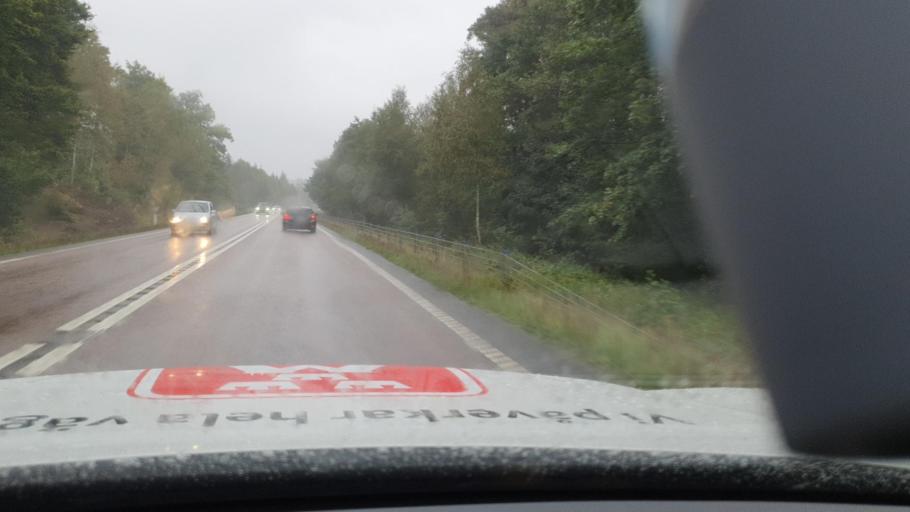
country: SE
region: Skane
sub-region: Klippans Kommun
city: Ljungbyhed
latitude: 56.1271
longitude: 13.2372
